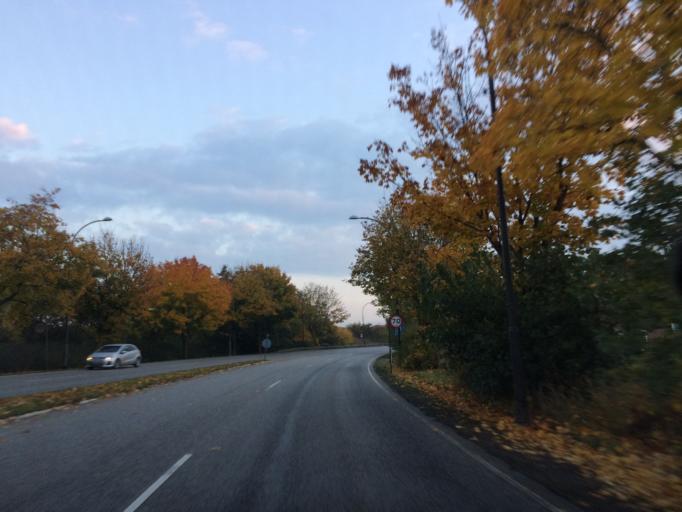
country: DK
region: Zealand
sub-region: Ringsted Kommune
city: Ringsted
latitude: 55.4472
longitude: 11.7806
